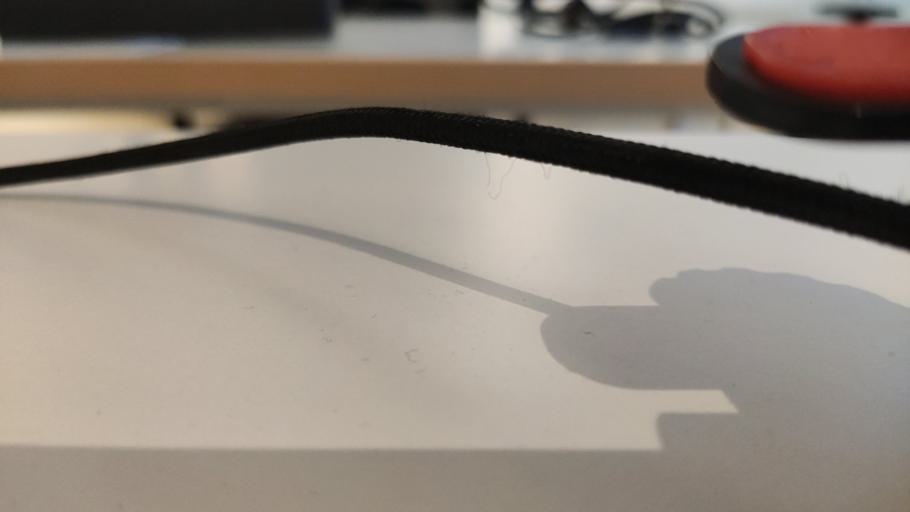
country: RU
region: Moskovskaya
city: Ruza
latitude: 55.7886
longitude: 36.2805
